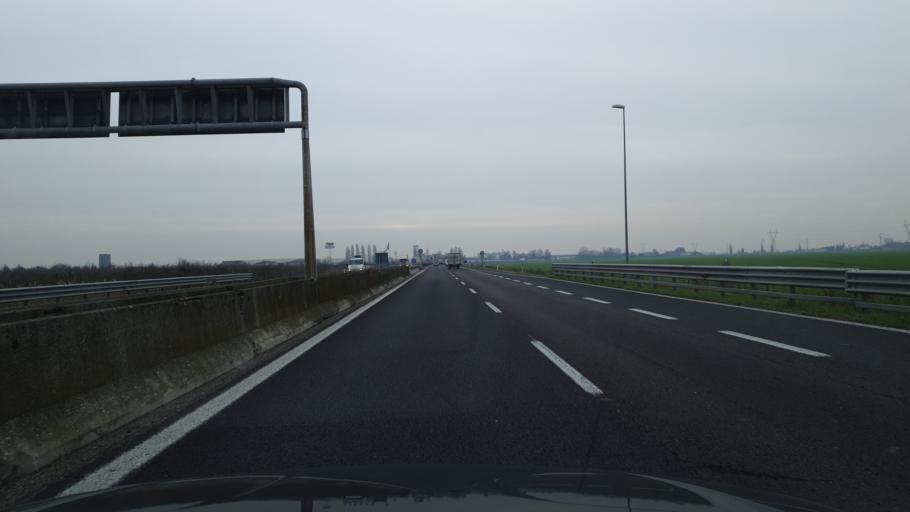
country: IT
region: Emilia-Romagna
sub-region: Provincia di Ferrara
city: San Martino
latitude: 44.7902
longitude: 11.5524
